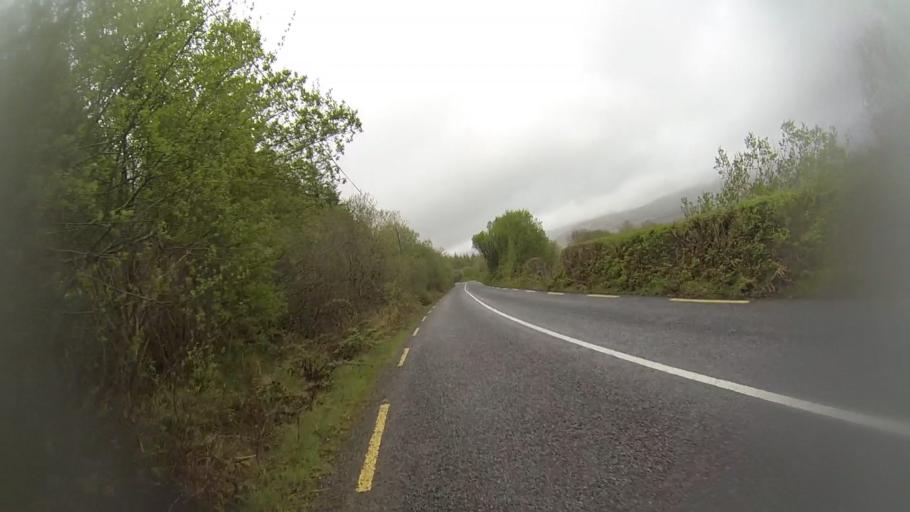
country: IE
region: Munster
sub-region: Ciarrai
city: Killorglin
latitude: 51.8548
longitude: -9.8551
